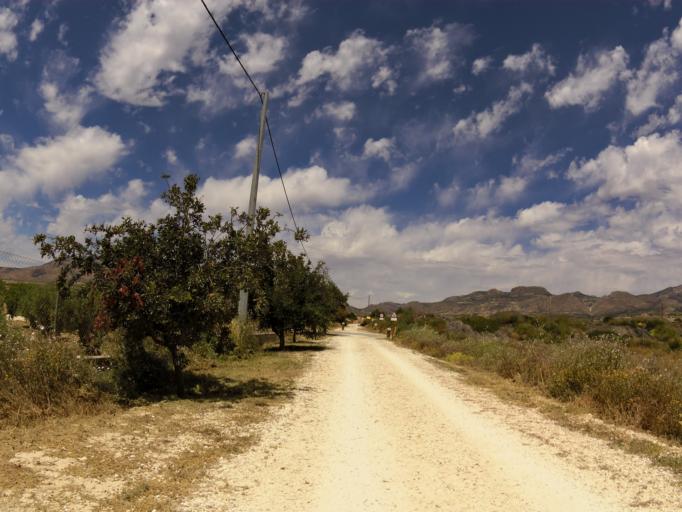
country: ES
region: Valencia
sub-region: Provincia de Alicante
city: Agost
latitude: 38.4378
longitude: -0.6474
